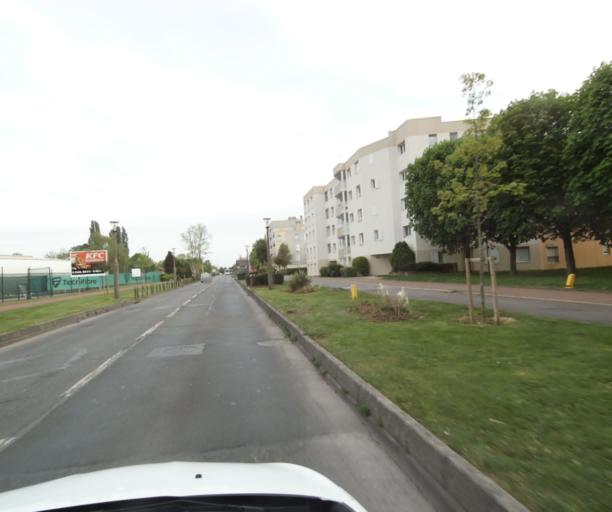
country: FR
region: Ile-de-France
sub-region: Departement de Seine-et-Marne
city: Torcy
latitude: 48.8460
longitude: 2.6529
